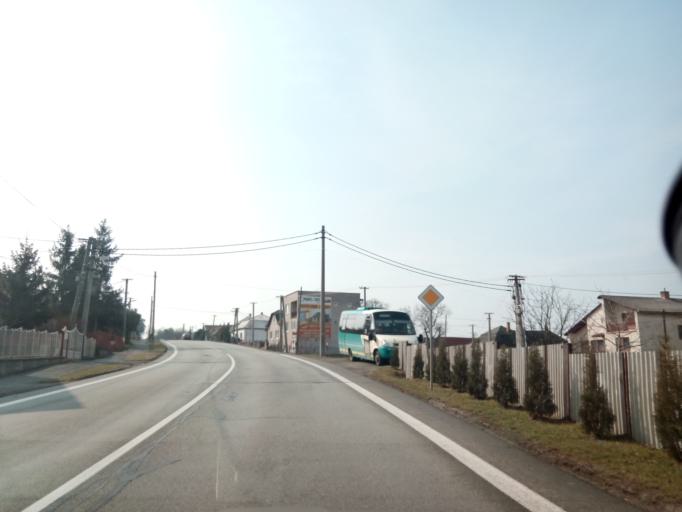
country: SK
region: Kosicky
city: Trebisov
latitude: 48.5210
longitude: 21.6611
